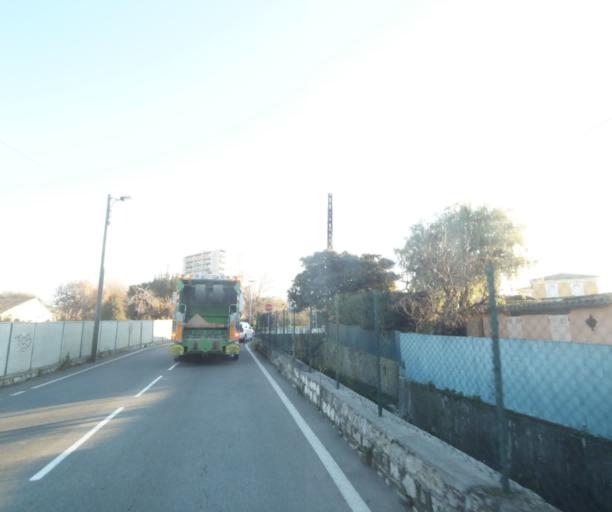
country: FR
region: Provence-Alpes-Cote d'Azur
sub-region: Departement des Alpes-Maritimes
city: Vallauris
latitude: 43.5757
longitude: 7.0868
